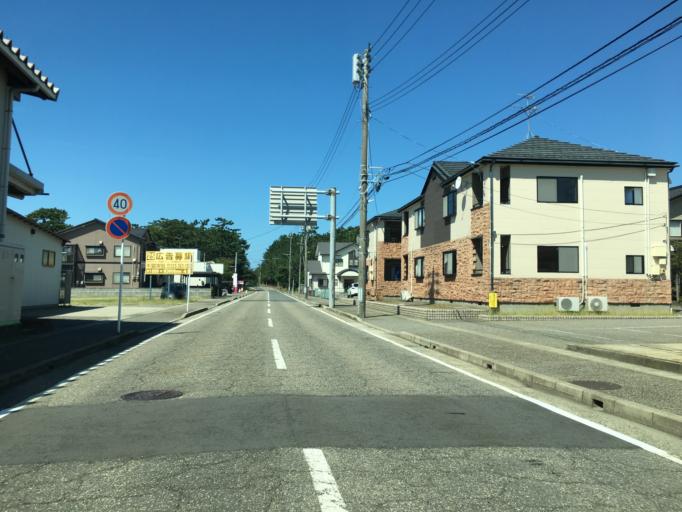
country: JP
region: Niigata
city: Niigata-shi
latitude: 37.8990
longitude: 138.9945
